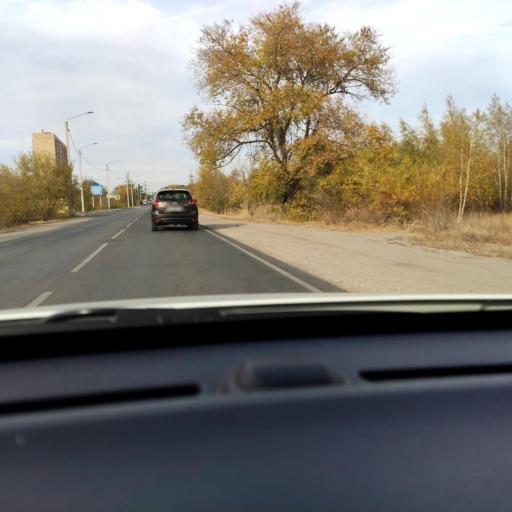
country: RU
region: Voronezj
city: Maslovka
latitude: 51.5858
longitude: 39.2479
